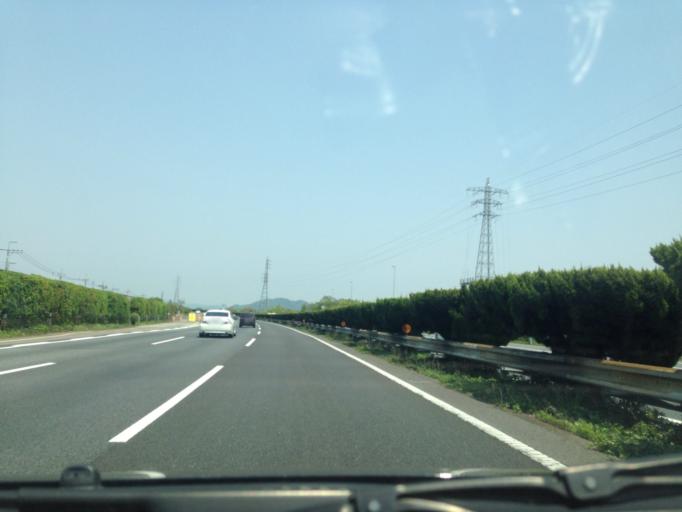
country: JP
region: Tochigi
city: Fujioka
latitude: 36.2582
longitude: 139.5986
